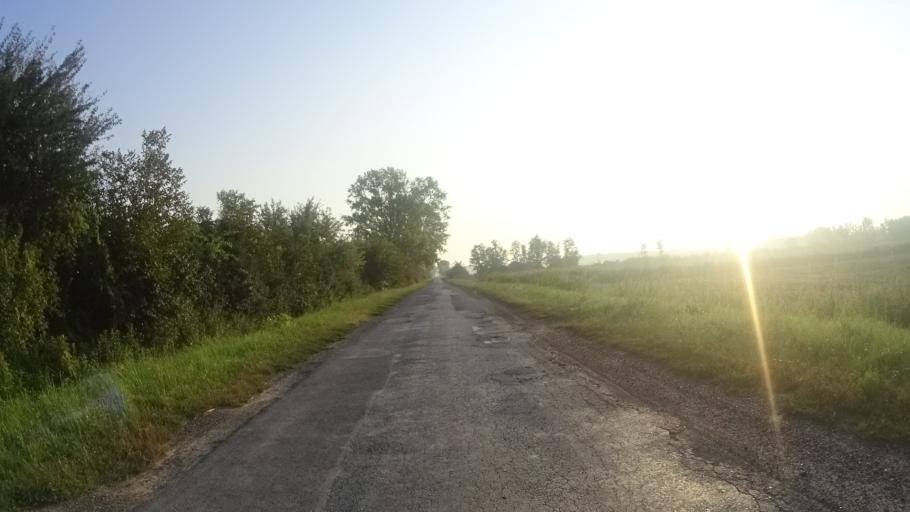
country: HU
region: Zala
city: Zalakomar
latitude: 46.5330
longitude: 17.1427
